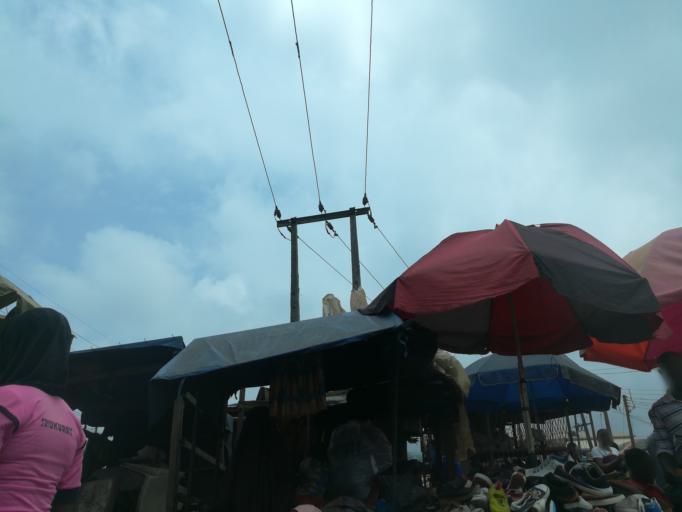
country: NG
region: Lagos
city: Ikorodu
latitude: 6.6629
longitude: 3.5195
